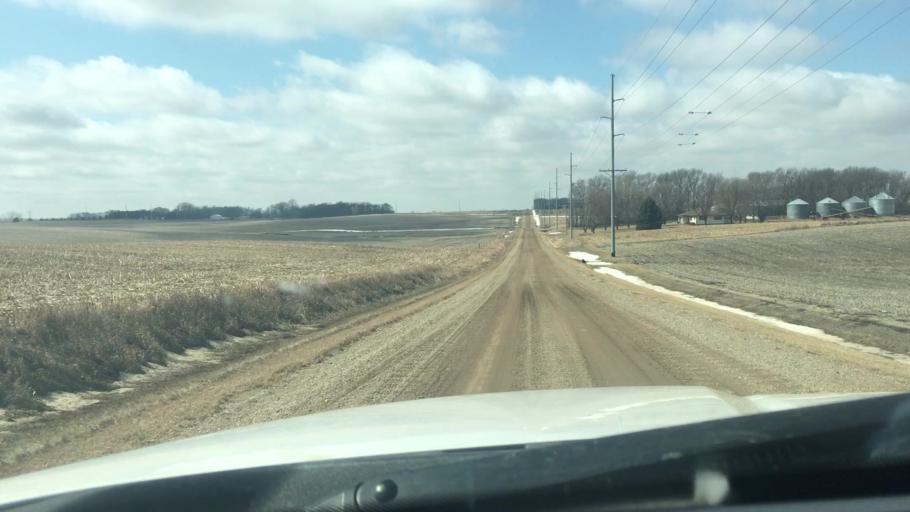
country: US
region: South Dakota
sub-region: Minnehaha County
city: Crooks
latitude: 43.6164
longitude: -96.7939
